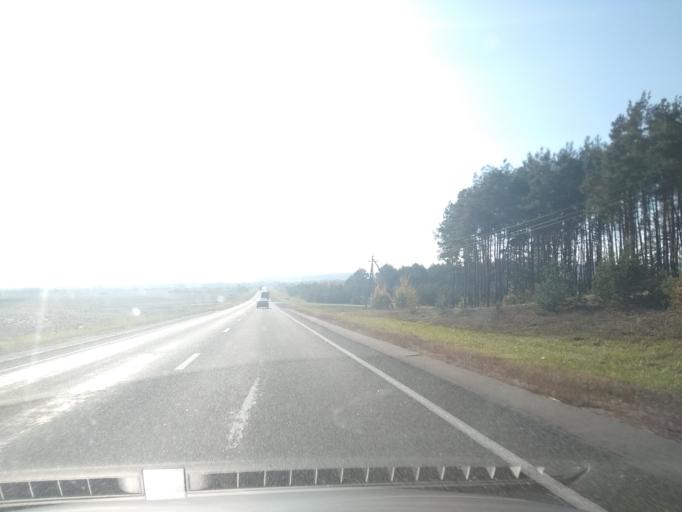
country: BY
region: Grodnenskaya
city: Zhyrovichy
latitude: 53.0573
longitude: 25.3844
